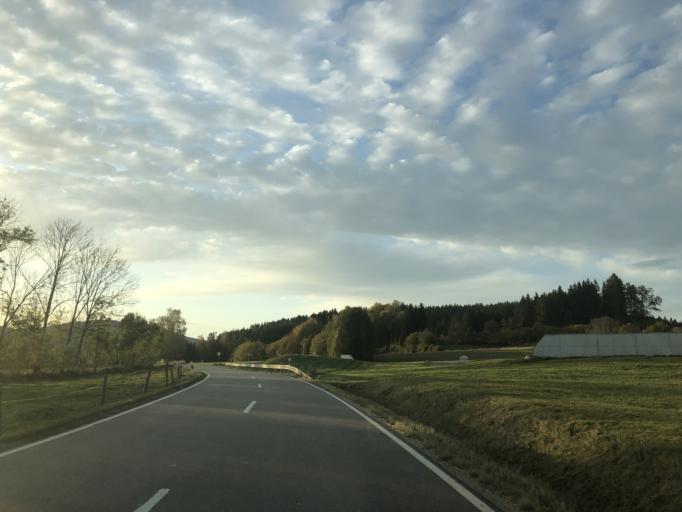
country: DE
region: Bavaria
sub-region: Lower Bavaria
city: Langdorf
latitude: 49.0160
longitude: 13.1872
